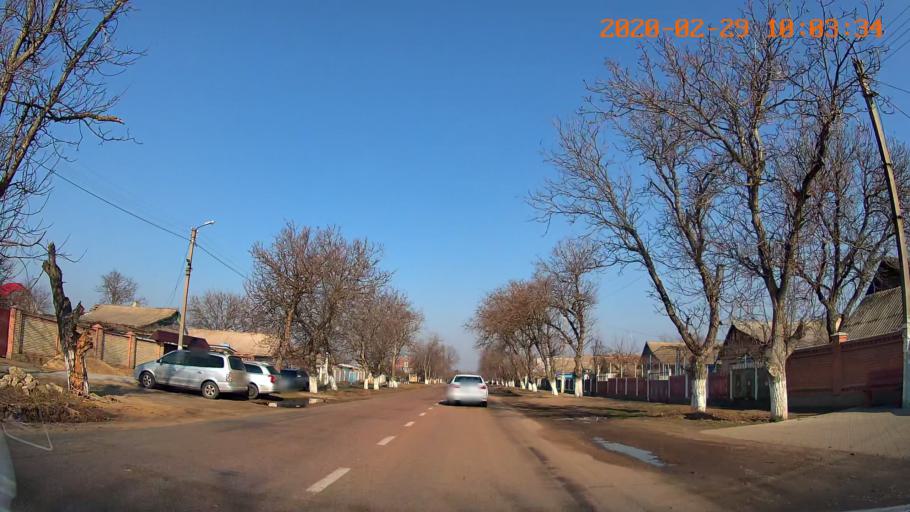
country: MD
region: Causeni
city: Chitcani
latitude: 46.7915
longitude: 29.6798
